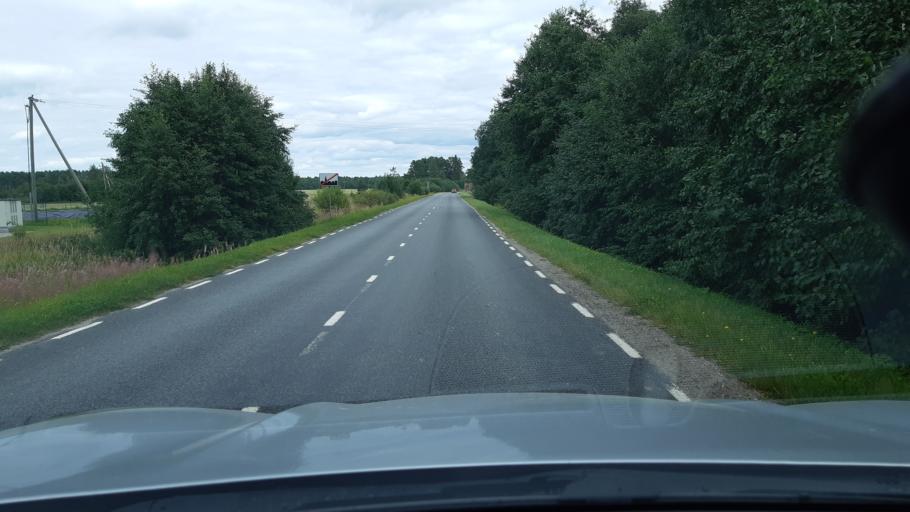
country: EE
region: Raplamaa
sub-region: Maerjamaa vald
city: Marjamaa
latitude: 59.0447
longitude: 24.4624
